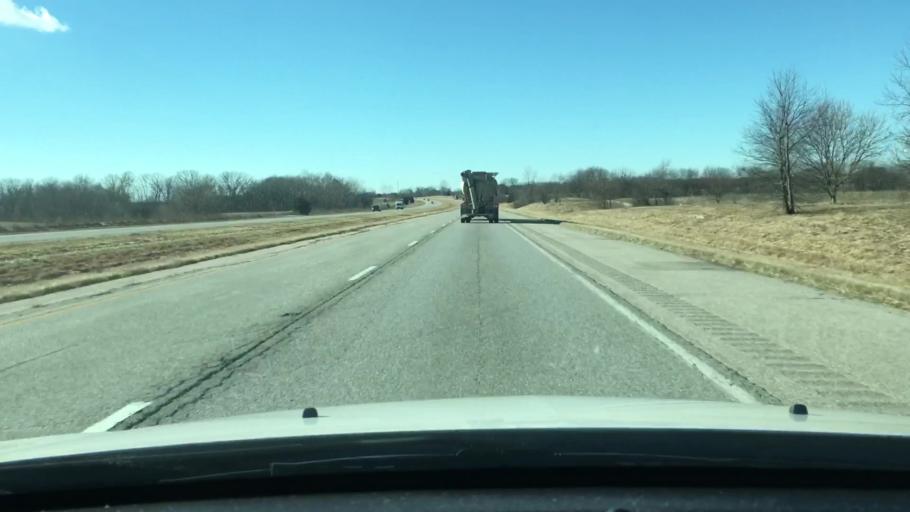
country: US
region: Illinois
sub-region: Pike County
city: Griggsville
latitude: 39.6784
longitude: -90.7143
